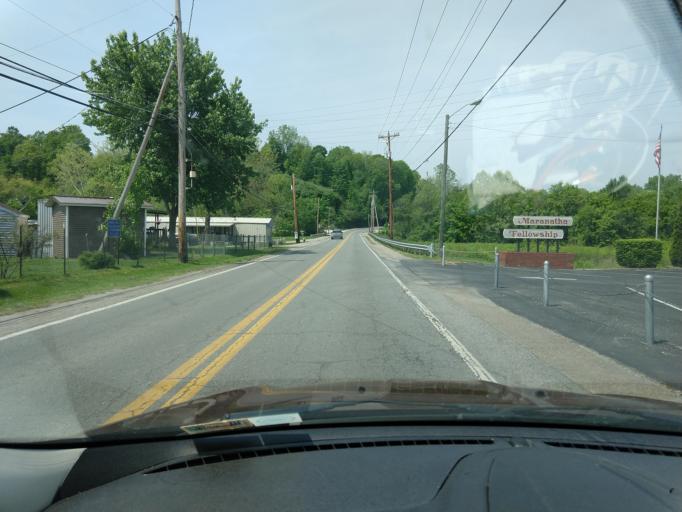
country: US
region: West Virginia
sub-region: Kanawha County
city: Saint Albans
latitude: 38.3754
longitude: -81.7934
